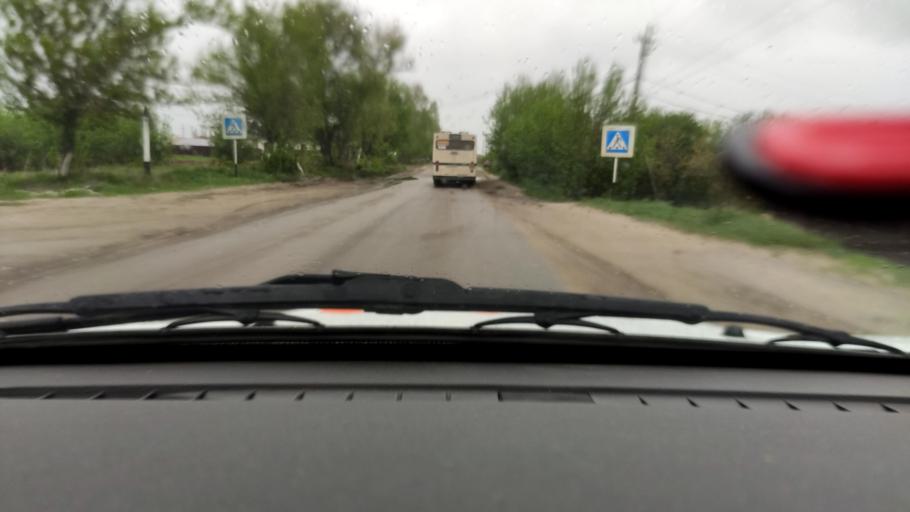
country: RU
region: Voronezj
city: Strelitsa
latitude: 51.6243
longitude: 38.9161
